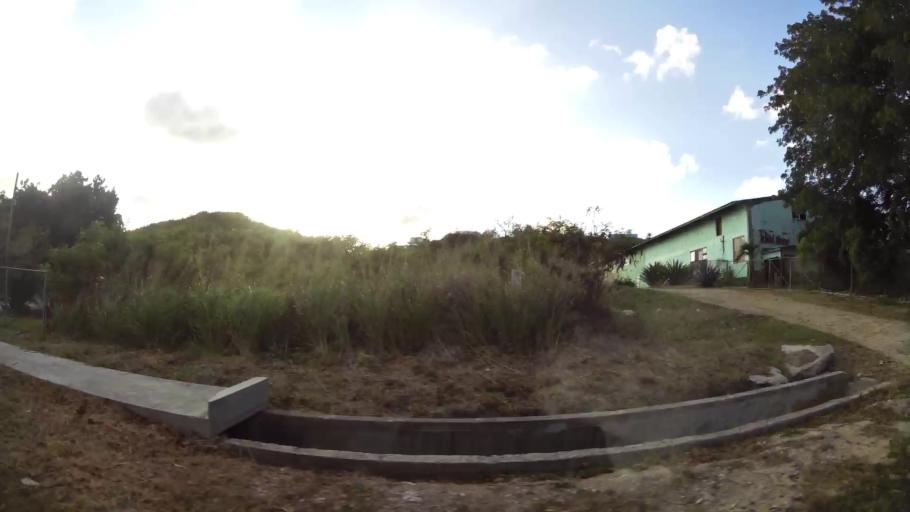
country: AG
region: Saint George
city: Piggotts
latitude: 17.1377
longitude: -61.7976
